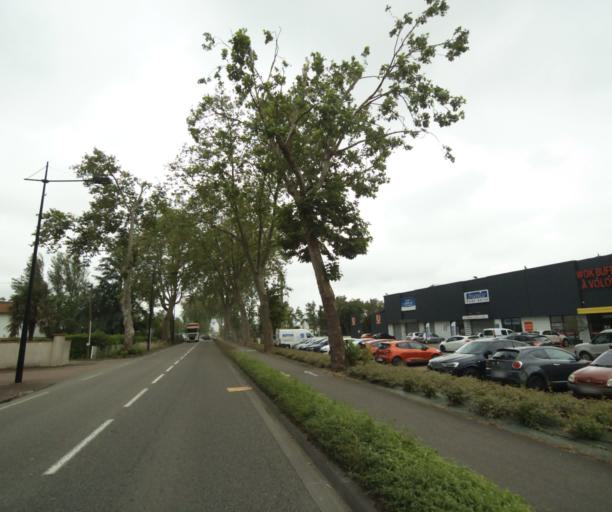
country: FR
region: Midi-Pyrenees
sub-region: Departement du Tarn-et-Garonne
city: Montauban
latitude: 43.9948
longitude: 1.3379
